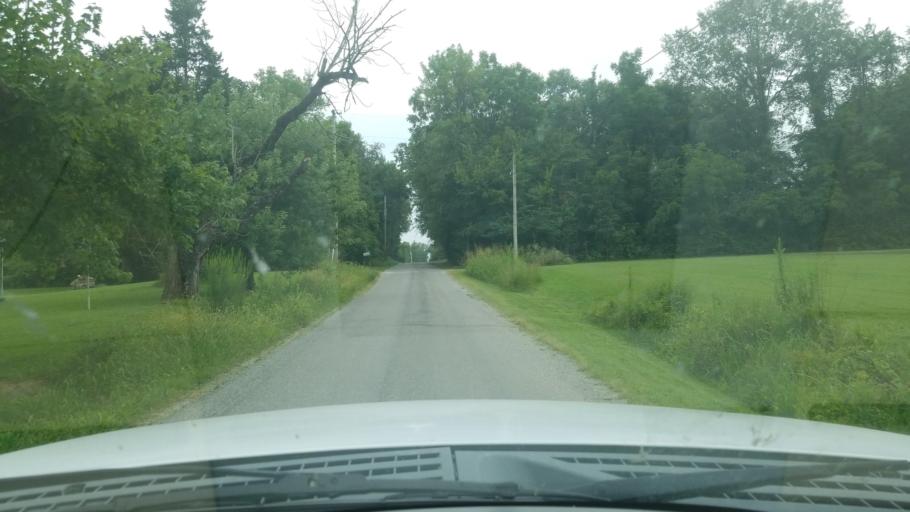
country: US
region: Illinois
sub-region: Saline County
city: Eldorado
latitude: 37.8275
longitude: -88.4477
